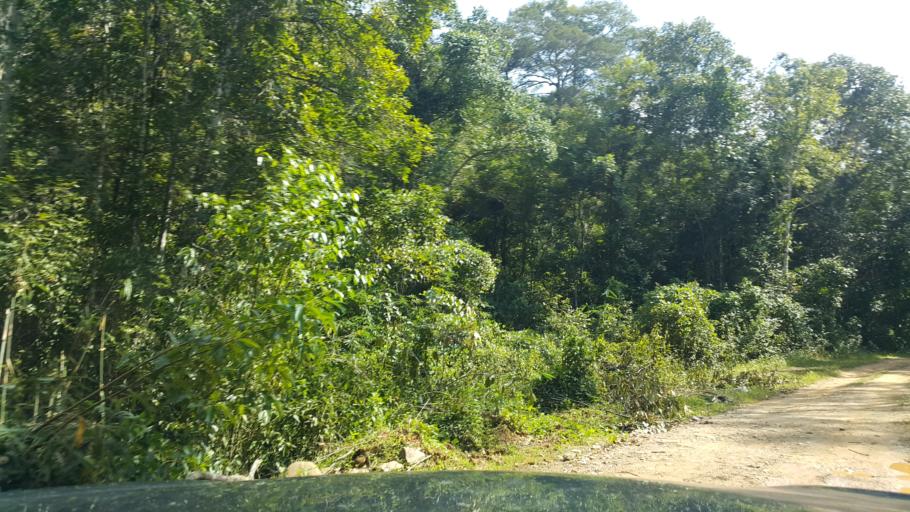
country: TH
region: Chiang Mai
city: Phrao
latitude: 19.0827
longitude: 99.2519
